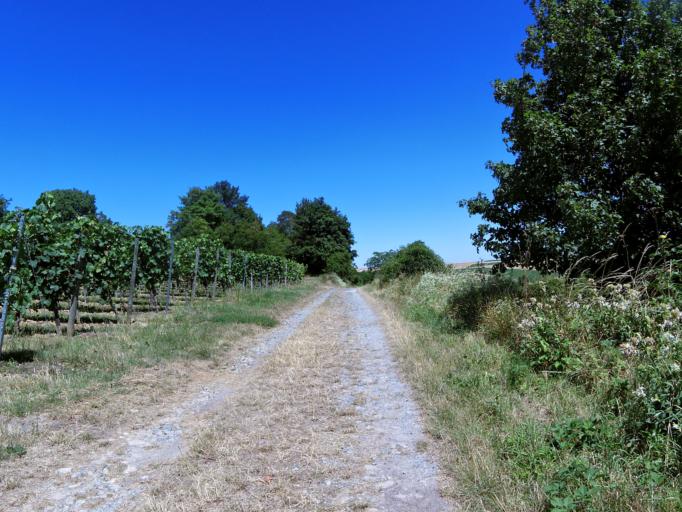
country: DE
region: Bavaria
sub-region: Regierungsbezirk Unterfranken
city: Gerbrunn
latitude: 49.7607
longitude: 10.0044
